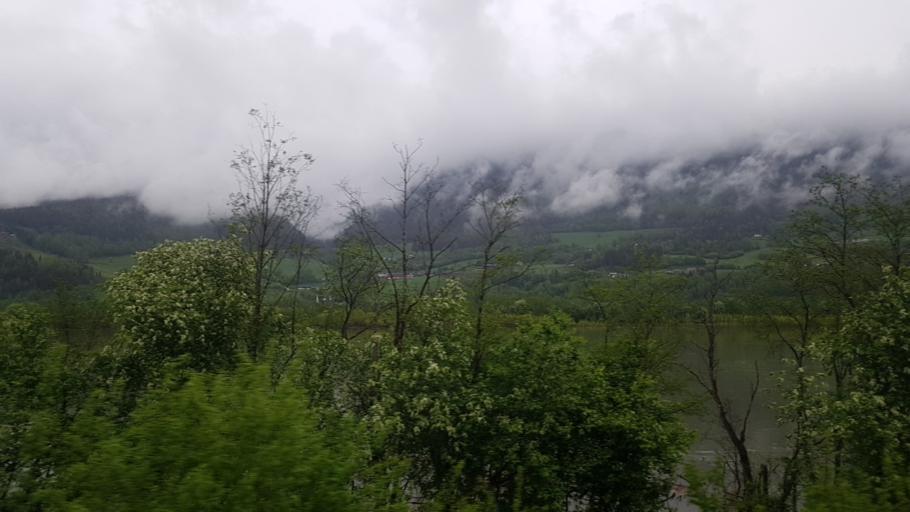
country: NO
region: Oppland
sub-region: Oyer
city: Tretten
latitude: 61.3940
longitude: 10.2497
